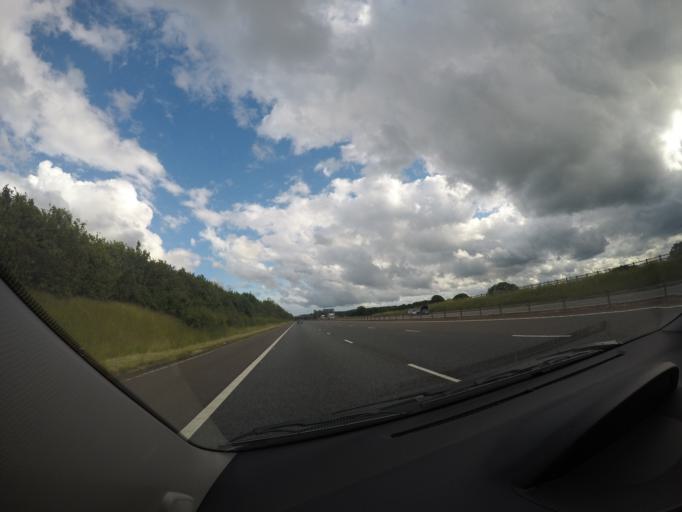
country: GB
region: Scotland
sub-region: Dumfries and Galloway
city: Lochmaben
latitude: 55.1874
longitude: -3.4070
